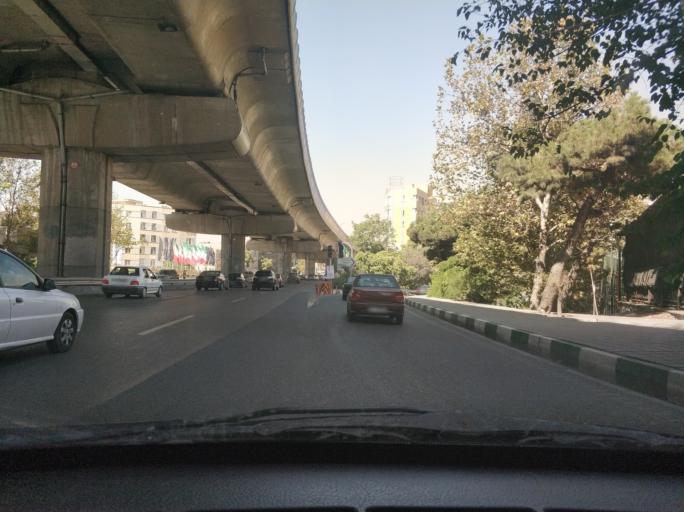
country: IR
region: Tehran
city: Tajrish
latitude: 35.7903
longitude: 51.4744
